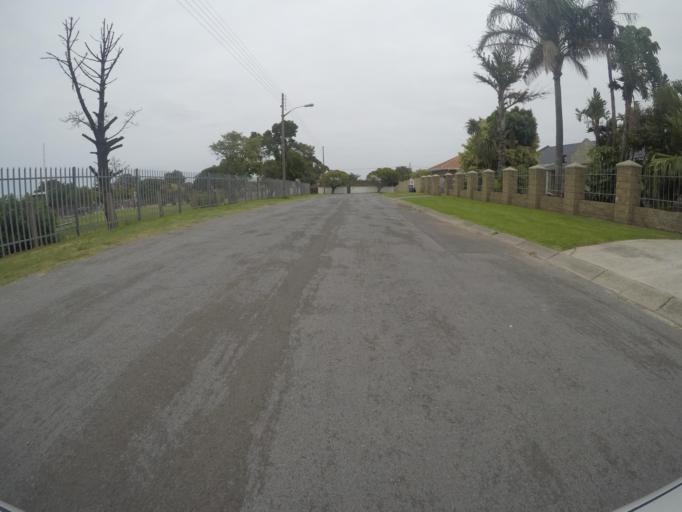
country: ZA
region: Eastern Cape
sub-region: Buffalo City Metropolitan Municipality
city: East London
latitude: -32.9693
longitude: 27.9357
